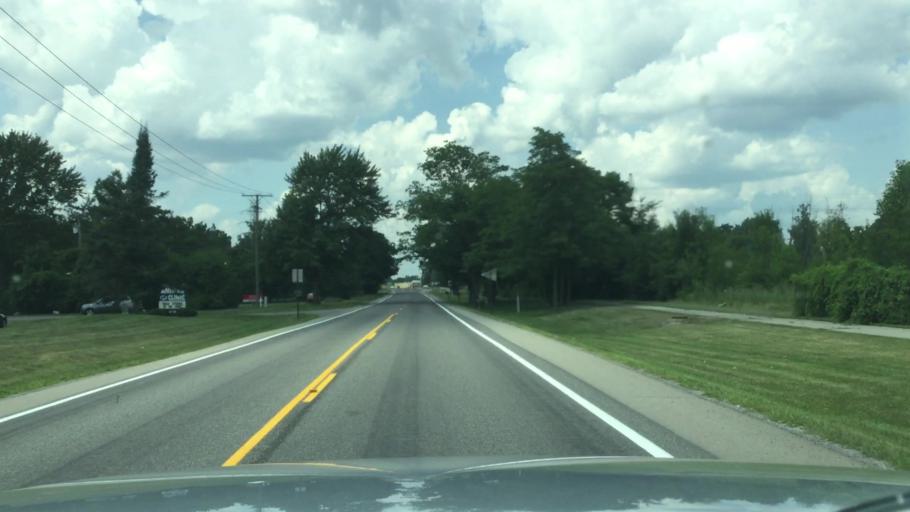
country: US
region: Michigan
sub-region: Washtenaw County
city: Ypsilanti
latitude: 42.2056
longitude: -83.6126
